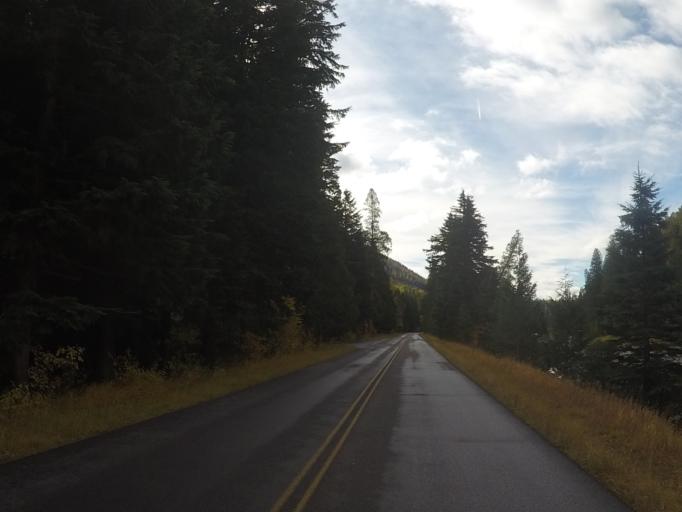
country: US
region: Montana
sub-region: Flathead County
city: Columbia Falls
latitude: 48.6523
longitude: -113.8404
